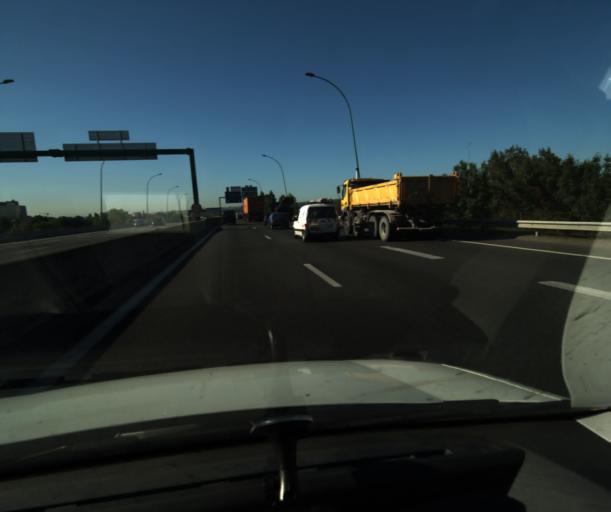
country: FR
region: Midi-Pyrenees
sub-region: Departement de la Haute-Garonne
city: Ramonville-Saint-Agne
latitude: 43.5659
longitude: 1.4936
